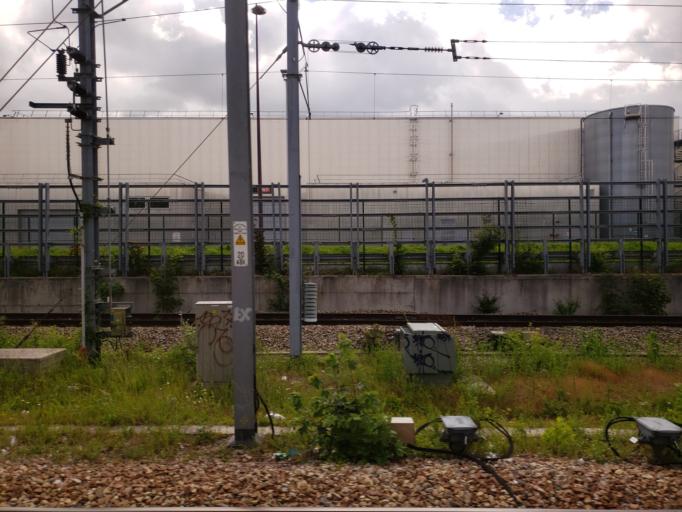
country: FR
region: Ile-de-France
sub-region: Departement de Seine-Saint-Denis
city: Villepinte
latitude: 48.9725
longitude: 2.5138
